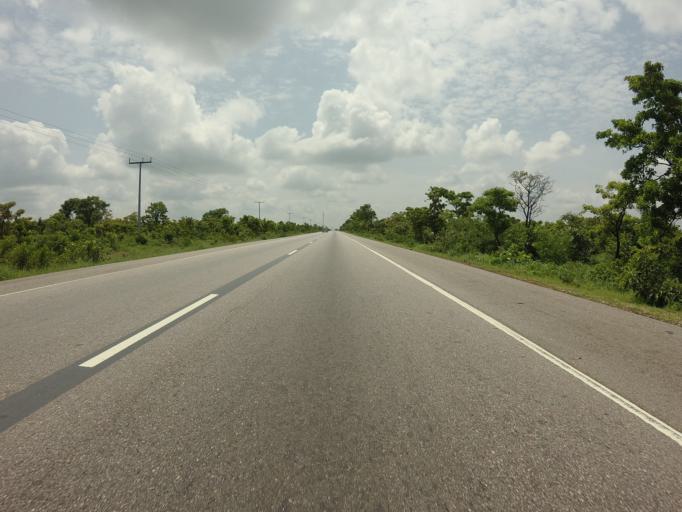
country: GH
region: Northern
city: Tamale
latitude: 9.1254
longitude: -1.2551
